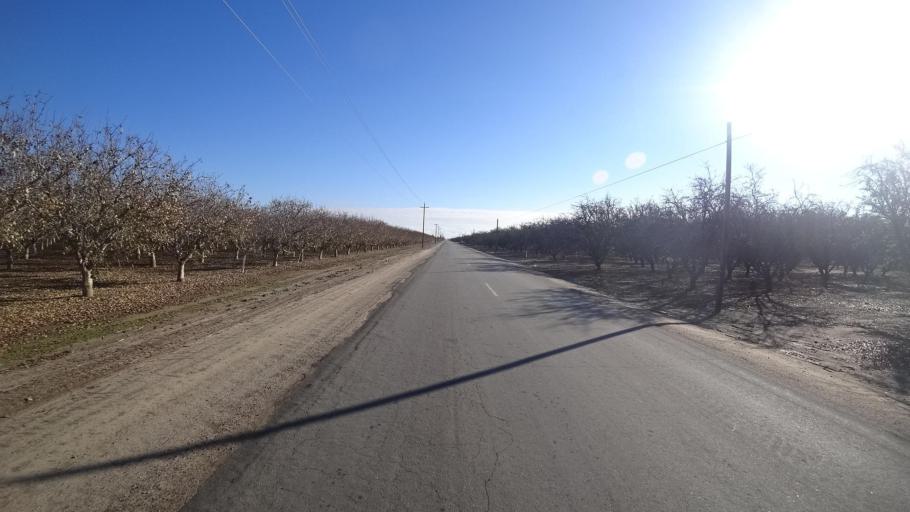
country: US
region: California
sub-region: Kern County
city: McFarland
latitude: 35.6887
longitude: -119.2977
